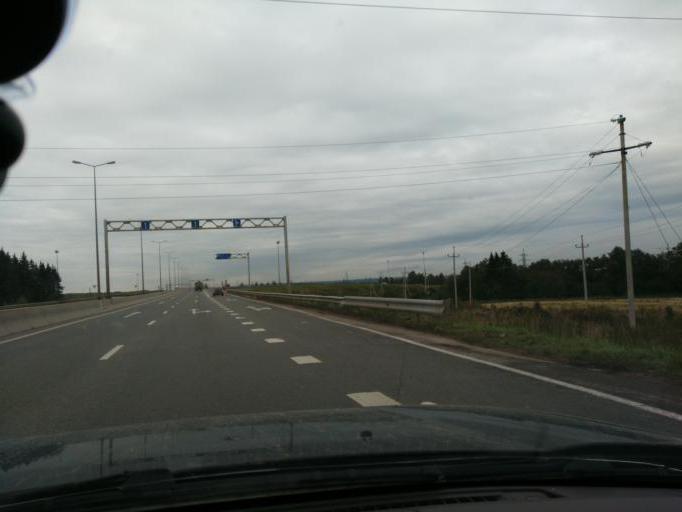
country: RU
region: Perm
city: Froly
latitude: 57.9334
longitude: 56.2592
